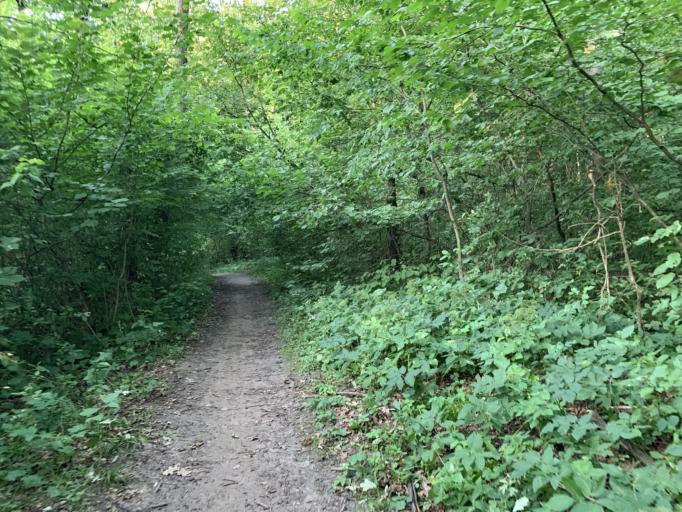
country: BY
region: Minsk
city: Nyasvizh
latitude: 53.2055
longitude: 26.6509
